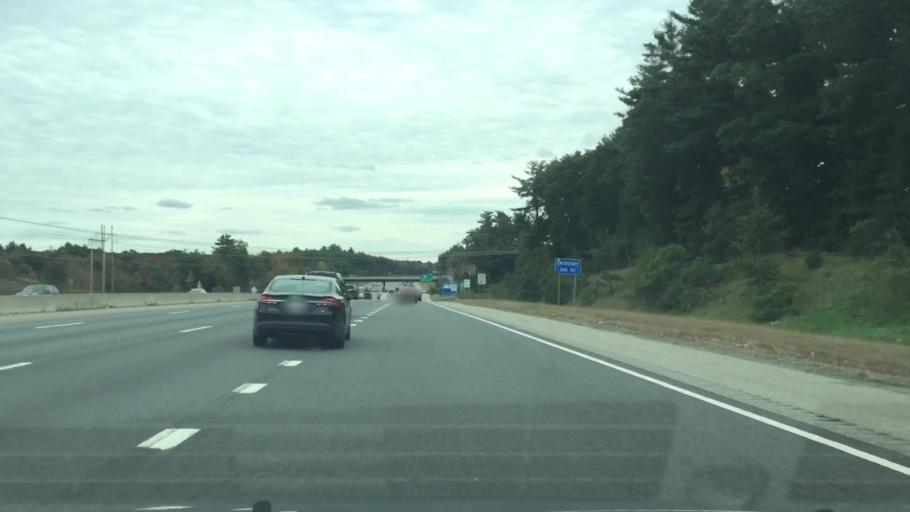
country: US
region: Massachusetts
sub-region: Middlesex County
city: Lowell
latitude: 42.5927
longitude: -71.3163
